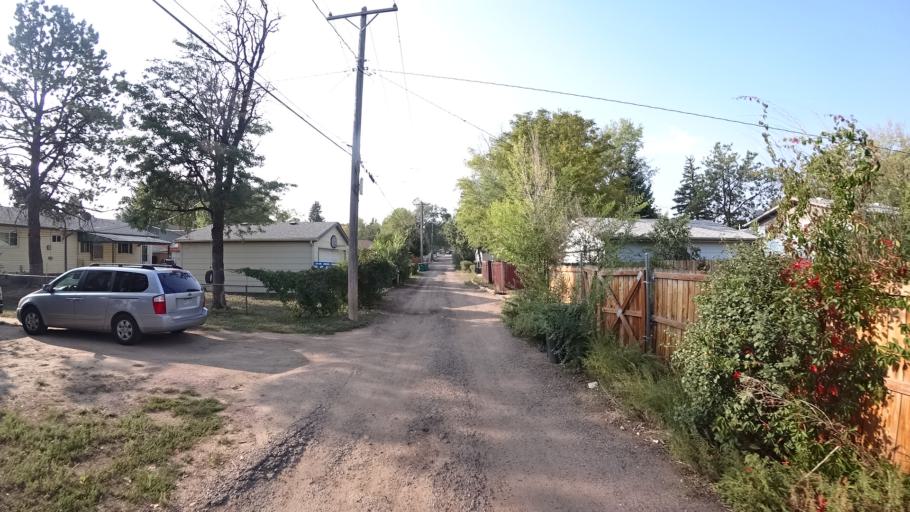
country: US
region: Colorado
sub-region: El Paso County
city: Colorado Springs
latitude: 38.8553
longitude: -104.7907
